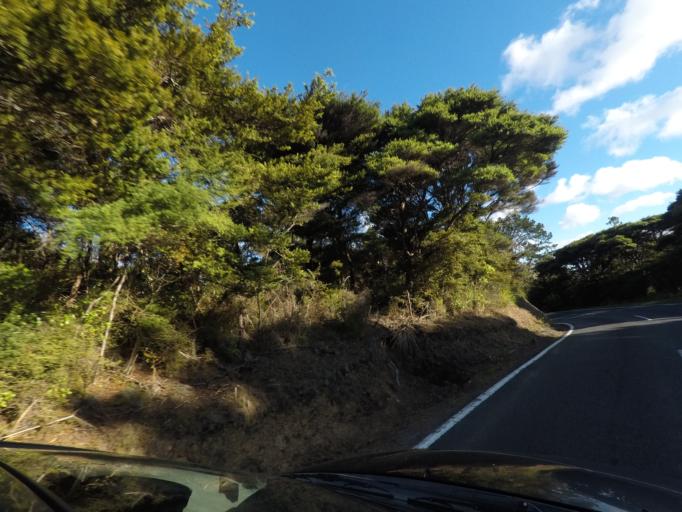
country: NZ
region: Auckland
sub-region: Auckland
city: Titirangi
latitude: -37.0070
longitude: 174.6013
